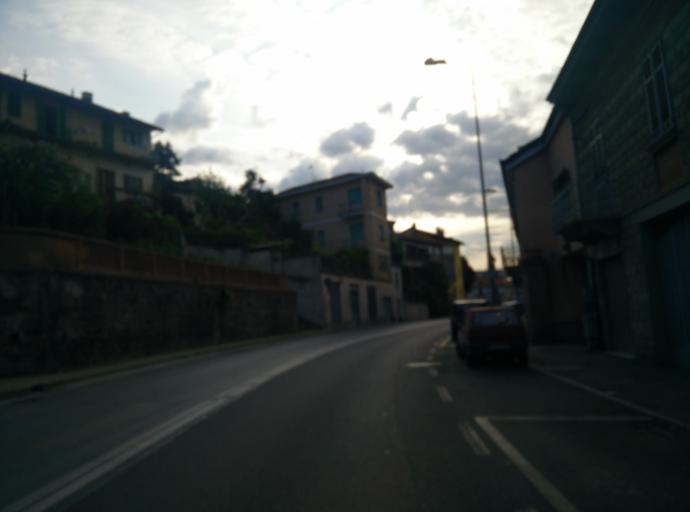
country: IT
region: Piedmont
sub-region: Provincia di Torino
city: Moncalieri
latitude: 45.0006
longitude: 7.6900
